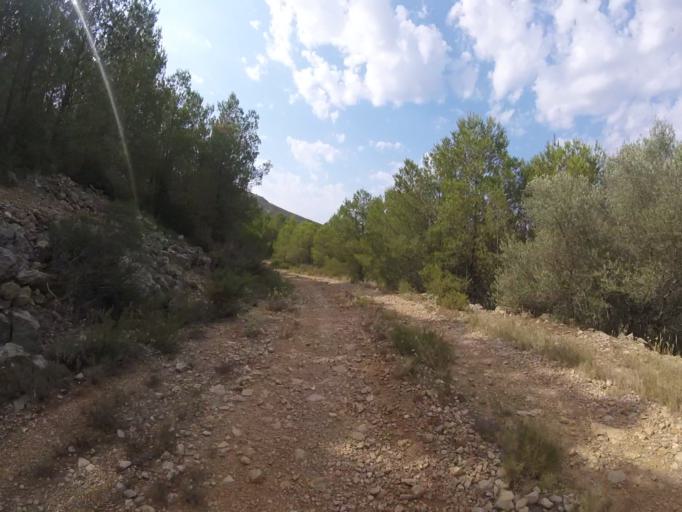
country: ES
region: Valencia
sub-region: Provincia de Castello
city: Alcala de Xivert
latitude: 40.3569
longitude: 0.1989
